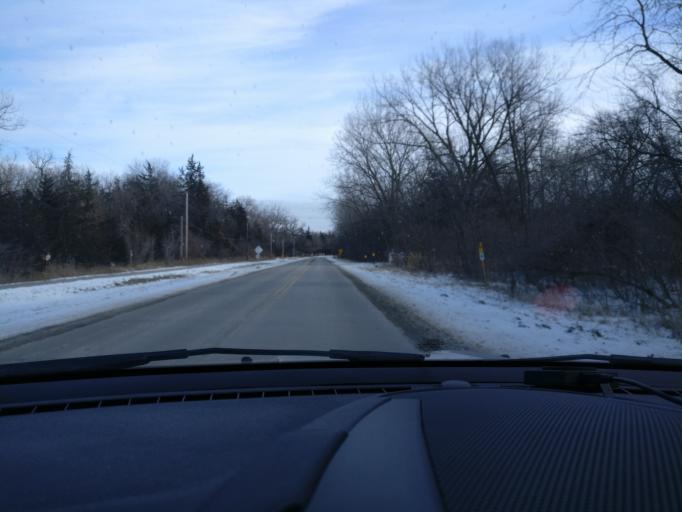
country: US
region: Nebraska
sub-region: Dodge County
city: Fremont
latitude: 41.4131
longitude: -96.5200
